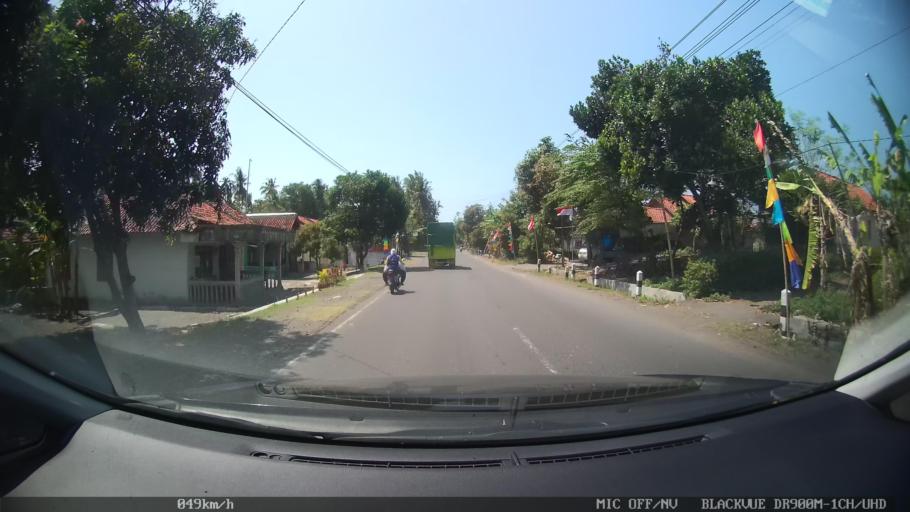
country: ID
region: Daerah Istimewa Yogyakarta
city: Srandakan
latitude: -7.9233
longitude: 110.1182
